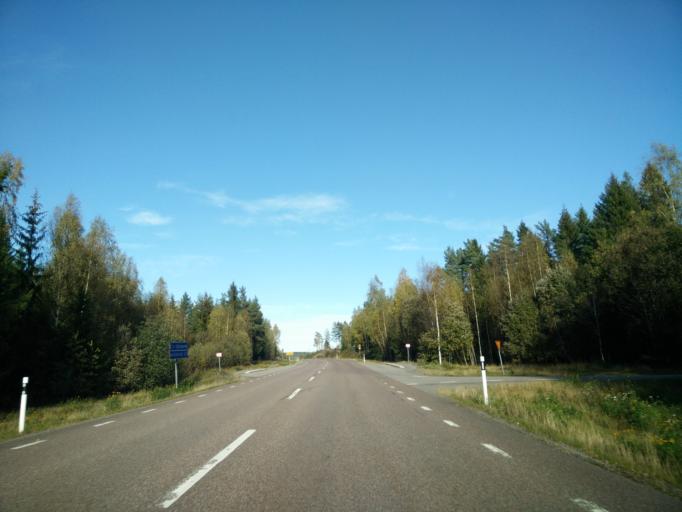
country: SE
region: Gaevleborg
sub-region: Hudiksvalls Kommun
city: Iggesund
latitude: 61.5573
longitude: 17.0132
